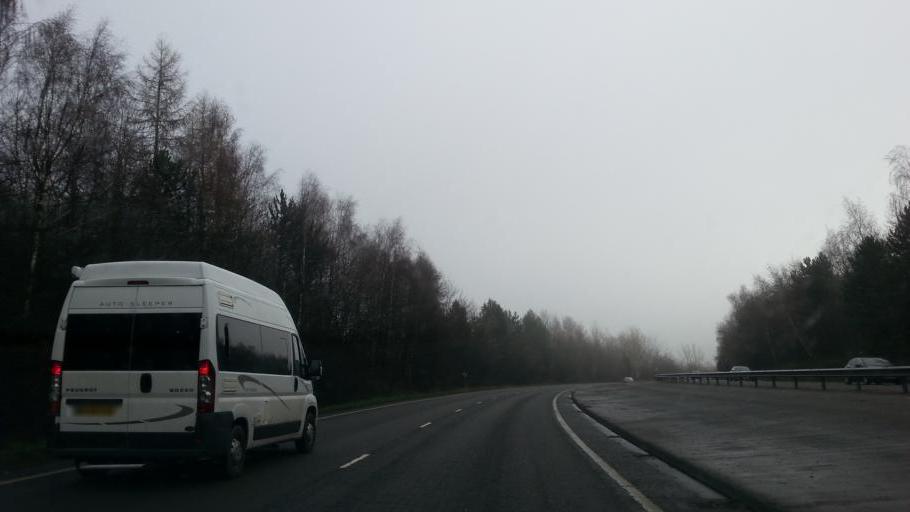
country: GB
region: England
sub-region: Cheshire East
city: Wilmslow
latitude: 53.3314
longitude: -2.2225
